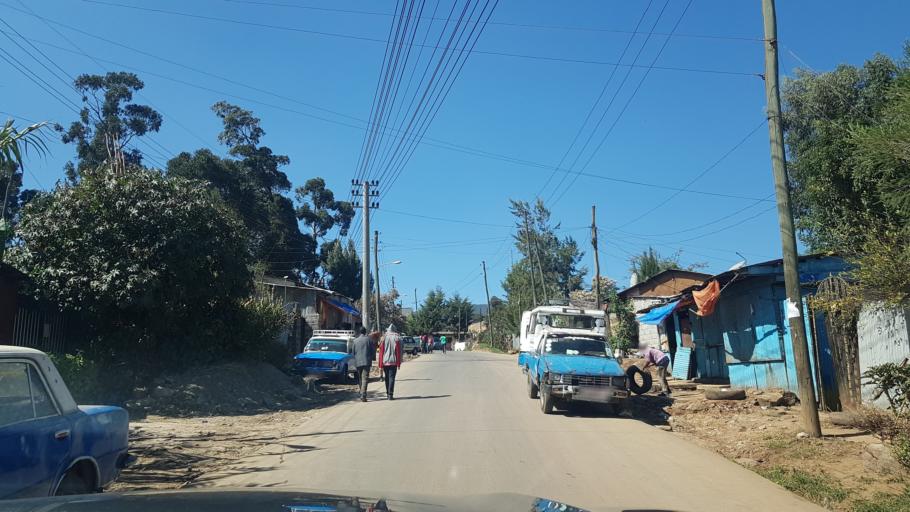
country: ET
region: Adis Abeba
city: Addis Ababa
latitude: 9.0534
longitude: 38.7497
